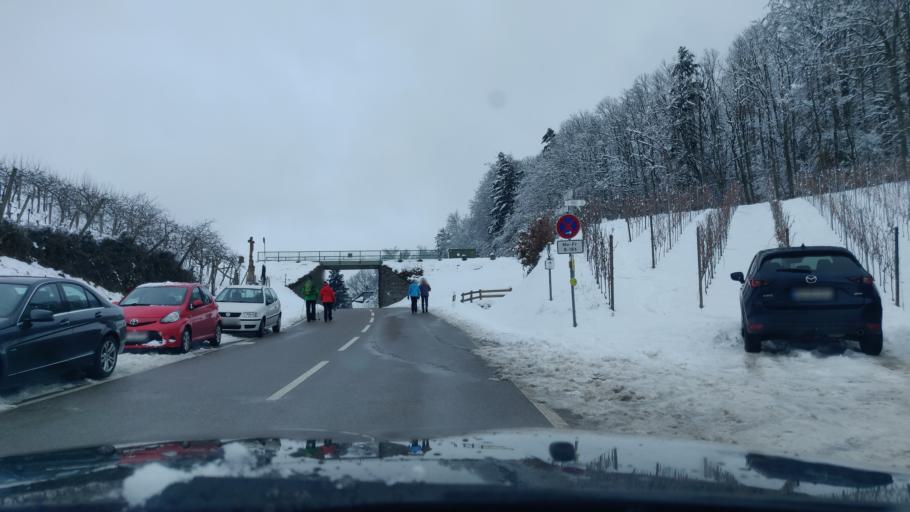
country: DE
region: Baden-Wuerttemberg
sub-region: Freiburg Region
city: Kappelrodeck
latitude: 48.5683
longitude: 8.0919
